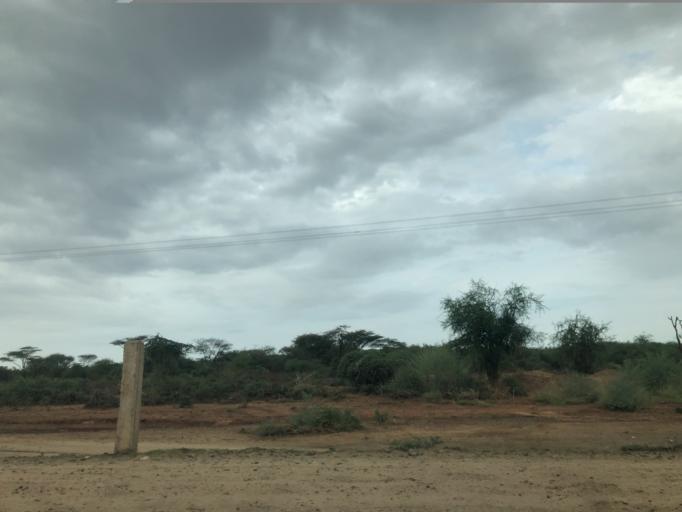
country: ET
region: Southern Nations, Nationalities, and People's Region
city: Turmi
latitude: 4.9944
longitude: 36.4727
